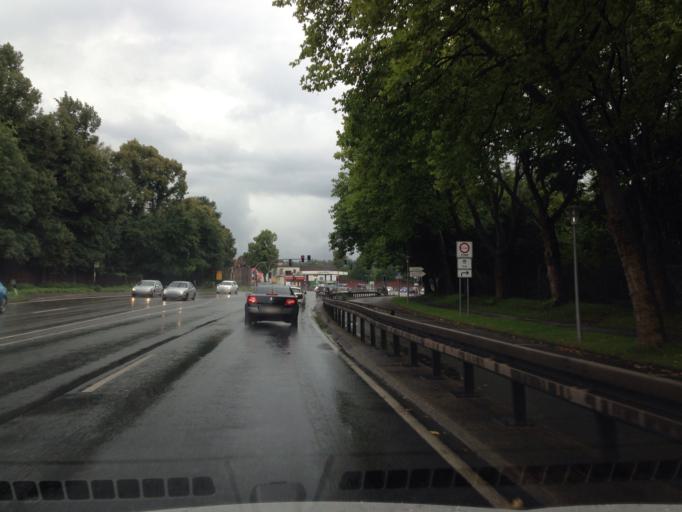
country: DE
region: North Rhine-Westphalia
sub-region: Regierungsbezirk Munster
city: Gladbeck
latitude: 51.5619
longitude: 6.9881
